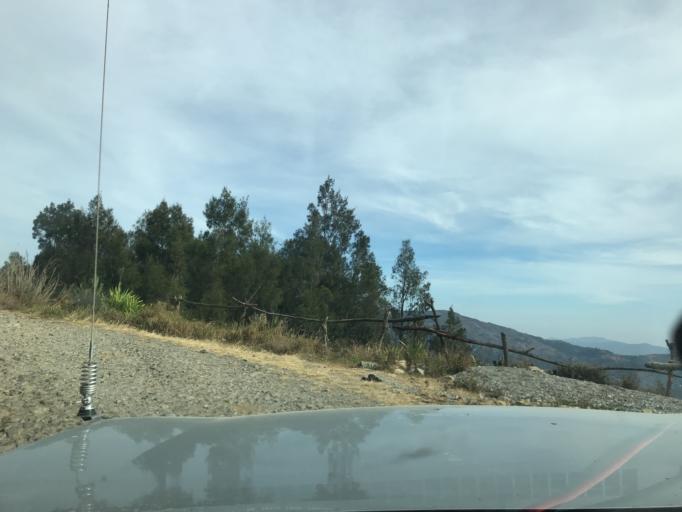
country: TL
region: Manufahi
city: Same
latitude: -8.8776
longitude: 125.5893
